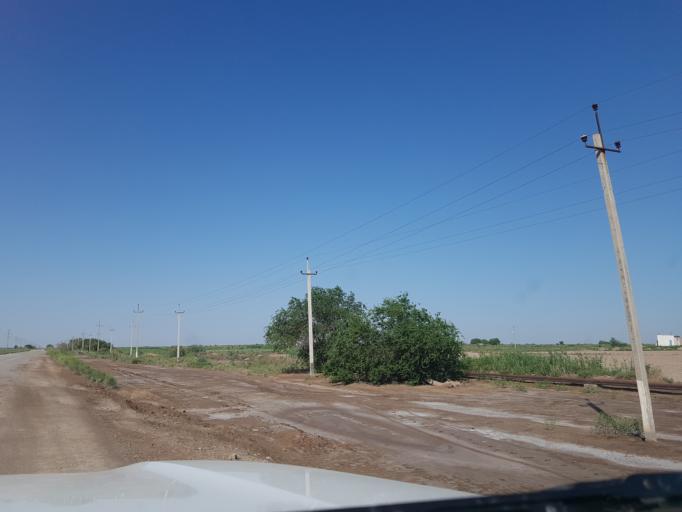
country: TM
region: Dasoguz
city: Koeneuergench
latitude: 42.1385
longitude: 58.9573
